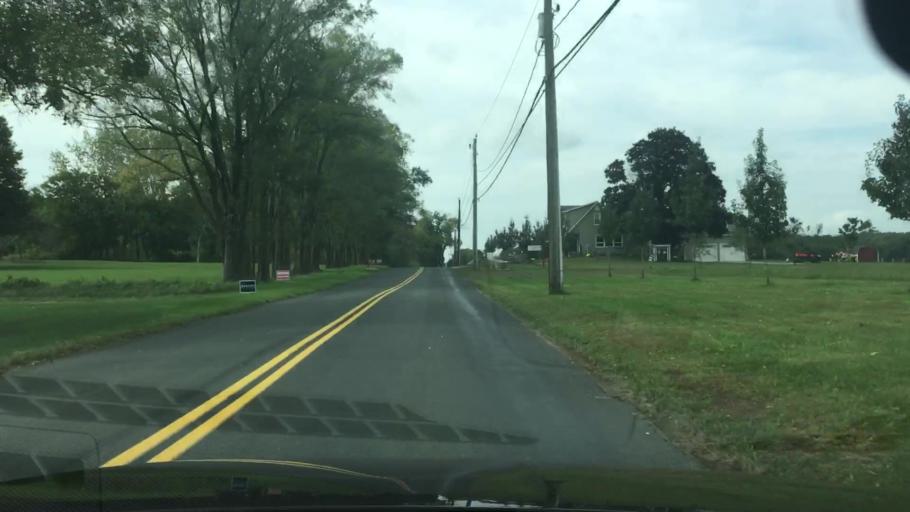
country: US
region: Connecticut
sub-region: Tolland County
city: Ellington
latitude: 41.9022
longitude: -72.4842
